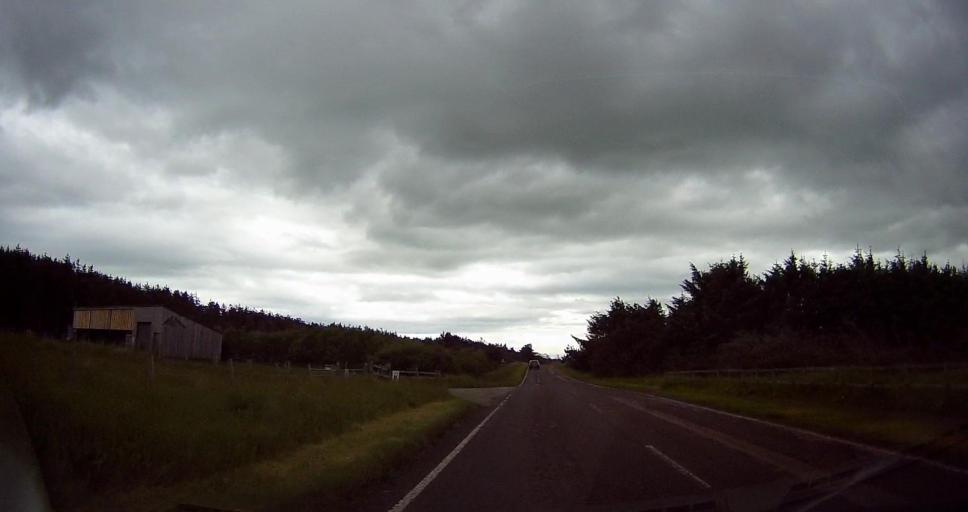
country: GB
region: Scotland
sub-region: Highland
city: Thurso
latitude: 58.6140
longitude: -3.3437
